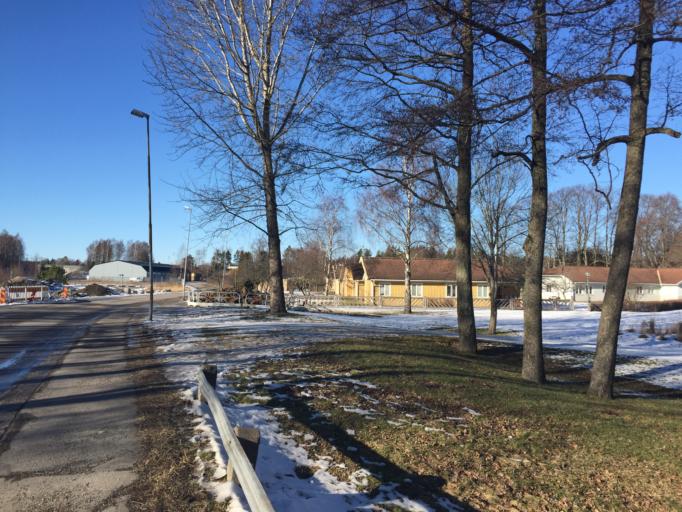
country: SE
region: Stockholm
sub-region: Nykvarns Kommun
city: Nykvarn
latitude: 59.1804
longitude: 17.4297
